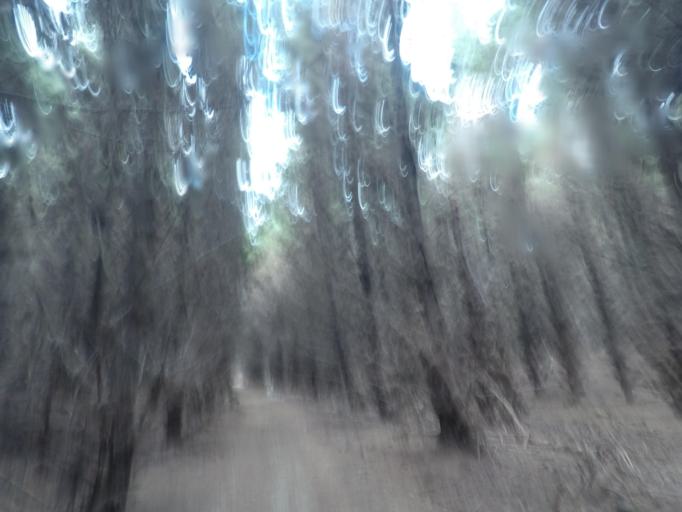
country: NZ
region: Auckland
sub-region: Auckland
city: Parakai
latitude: -36.6021
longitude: 174.2735
